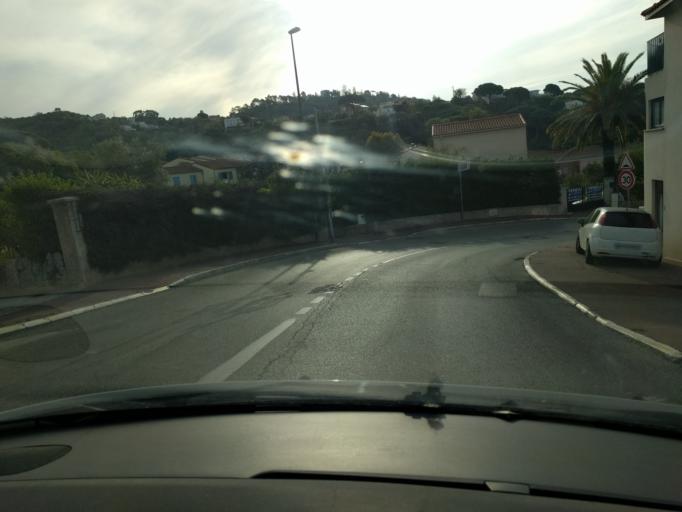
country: FR
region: Provence-Alpes-Cote d'Azur
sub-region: Departement des Alpes-Maritimes
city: Cannes
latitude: 43.5589
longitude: 6.9736
